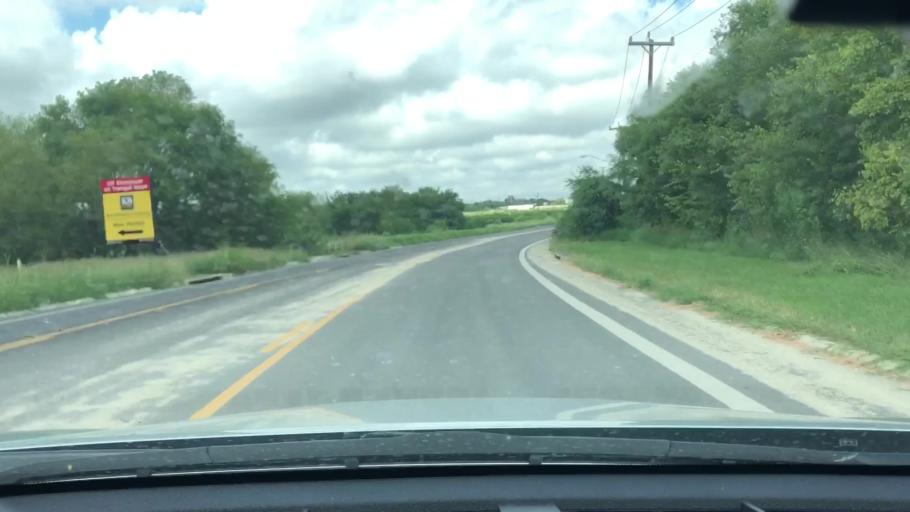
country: US
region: Texas
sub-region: Bexar County
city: Windcrest
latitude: 29.5006
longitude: -98.3678
